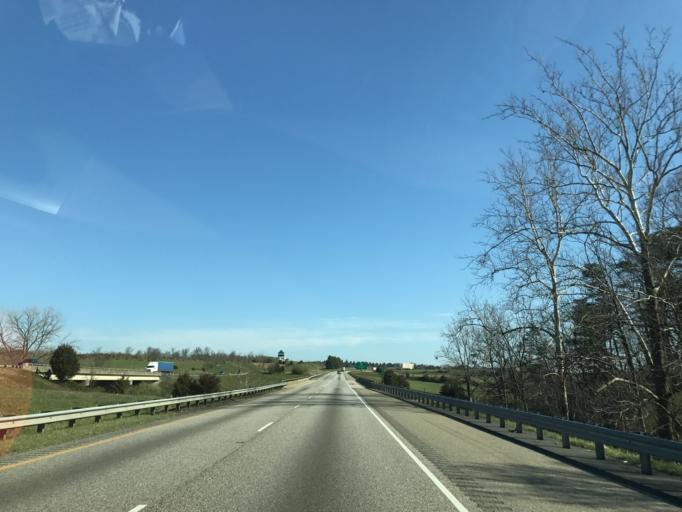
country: US
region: Virginia
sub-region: Augusta County
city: Verona
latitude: 38.1575
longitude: -79.0147
